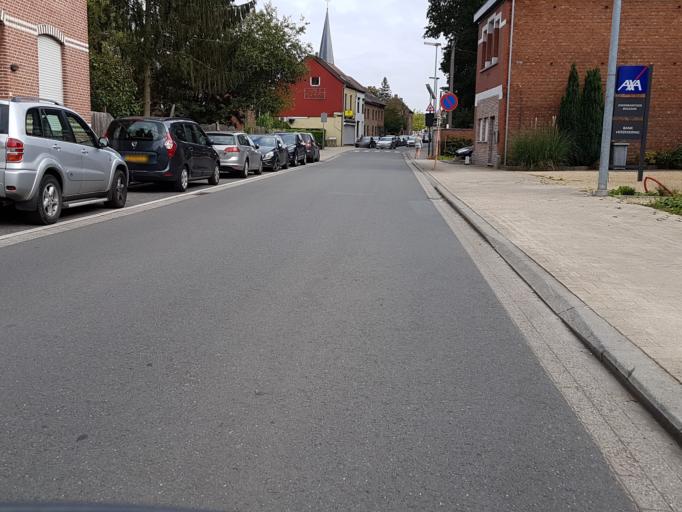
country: BE
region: Flanders
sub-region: Provincie Vlaams-Brabant
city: Haacht
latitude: 50.9598
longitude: 4.6306
